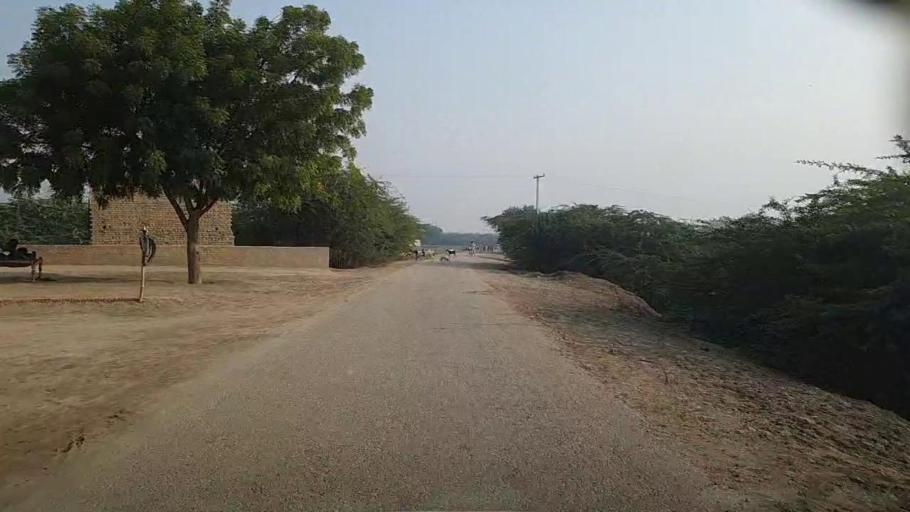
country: PK
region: Sindh
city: Kandiari
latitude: 27.0416
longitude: 68.4771
